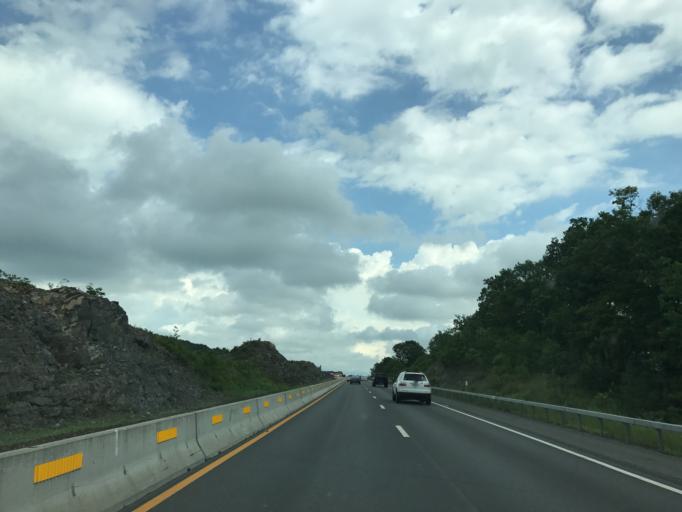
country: US
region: New York
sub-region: Greene County
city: Jefferson Heights
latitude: 42.2731
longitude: -73.8735
